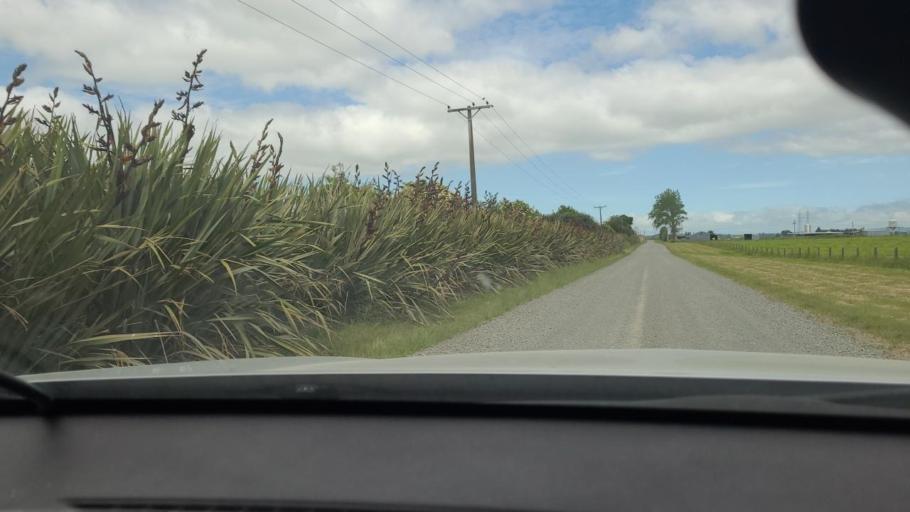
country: NZ
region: Southland
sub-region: Southland District
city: Winton
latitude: -46.0434
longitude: 168.0576
